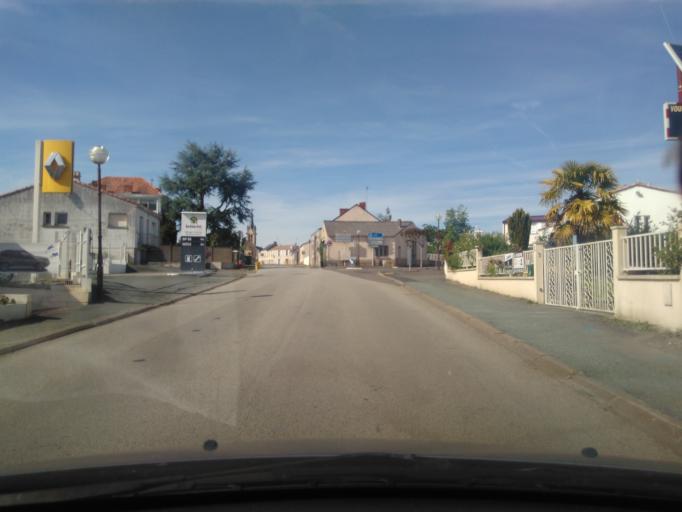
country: FR
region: Pays de la Loire
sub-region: Departement de la Vendee
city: Nieul-le-Dolent
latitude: 46.5725
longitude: -1.5099
